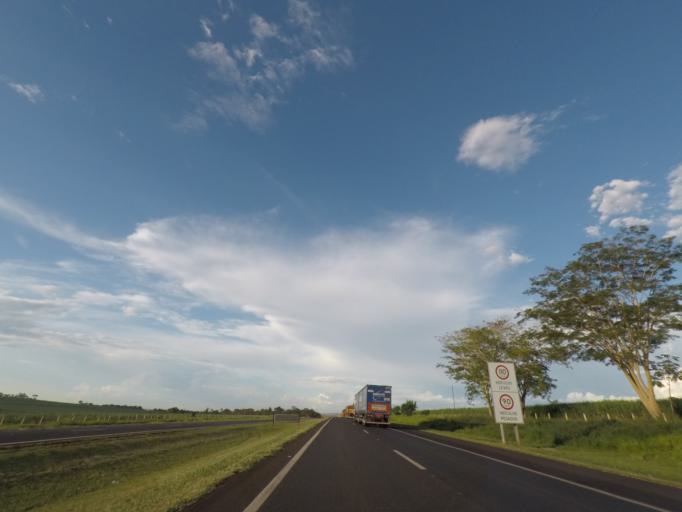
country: BR
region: Sao Paulo
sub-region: Ituverava
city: Ituverava
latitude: -20.3109
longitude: -47.8012
